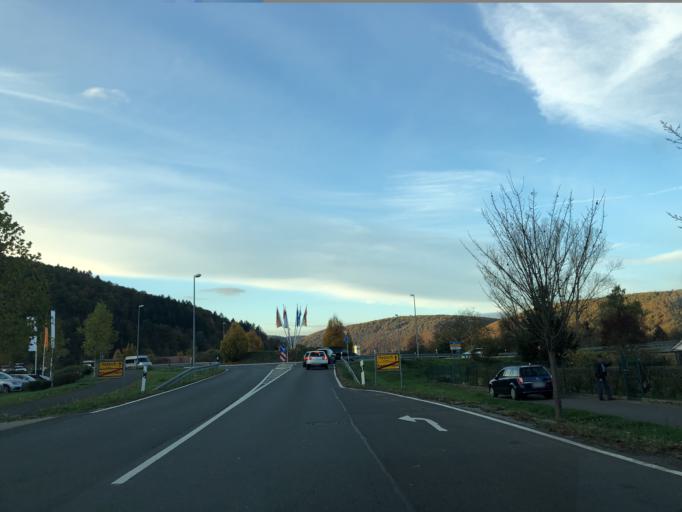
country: DE
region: Bavaria
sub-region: Regierungsbezirk Unterfranken
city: Kreuzwertheim
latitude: 49.7694
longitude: 9.5134
